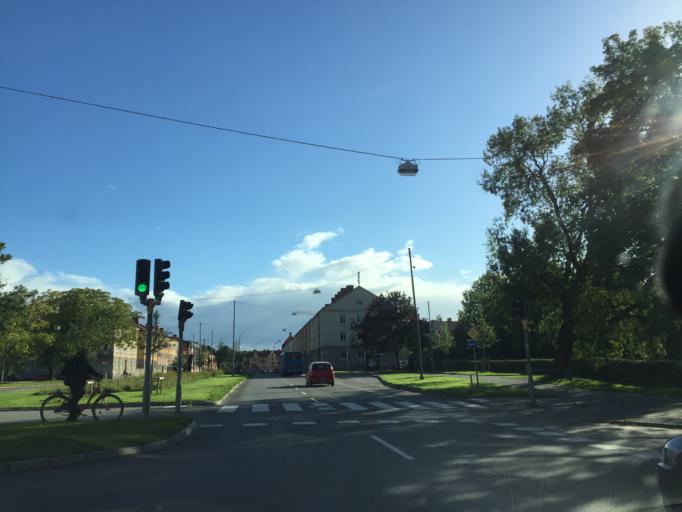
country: SE
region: OErebro
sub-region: Orebro Kommun
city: Orebro
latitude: 59.2772
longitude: 15.2008
